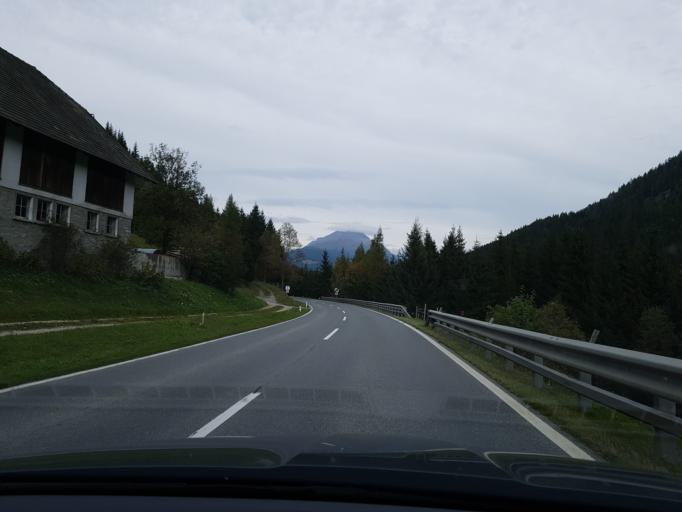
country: AT
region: Salzburg
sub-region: Politischer Bezirk Tamsweg
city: Tamsweg
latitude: 47.1069
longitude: 13.8173
